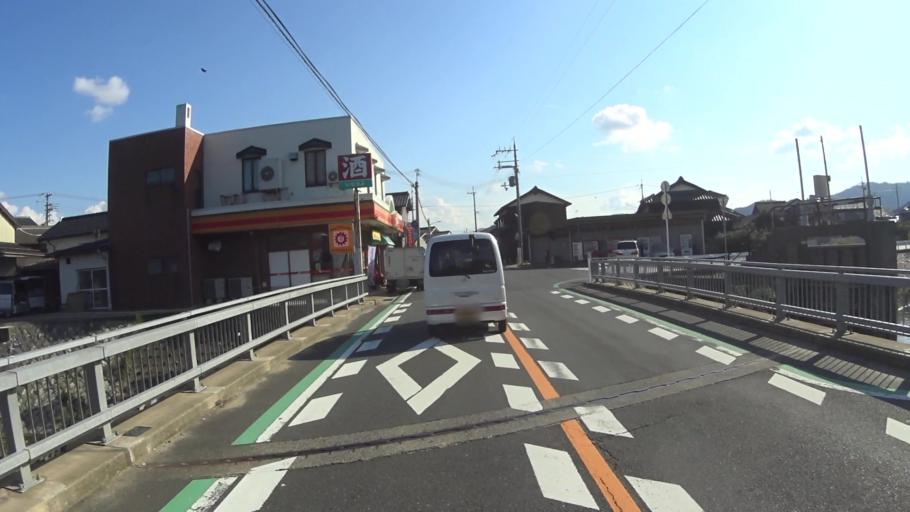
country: JP
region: Kyoto
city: Miyazu
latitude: 35.6906
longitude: 135.0350
